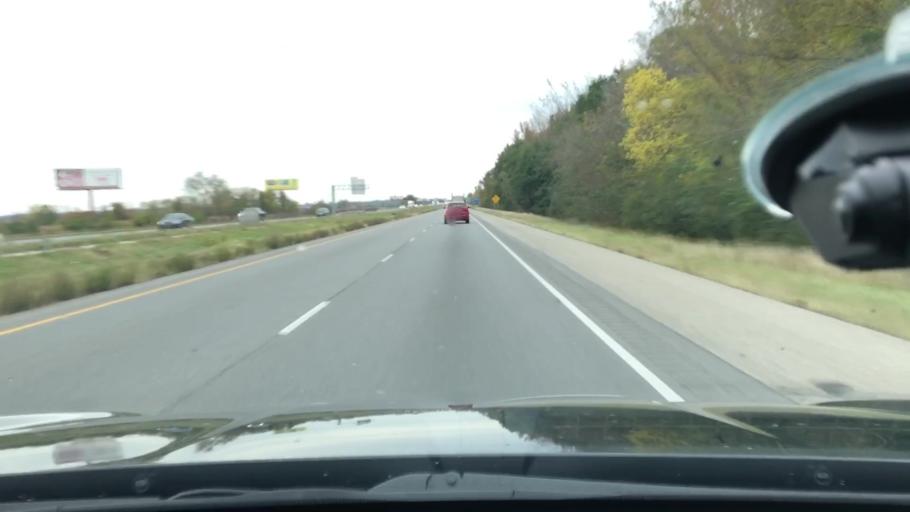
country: US
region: Arkansas
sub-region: Miller County
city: Texarkana
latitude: 33.4914
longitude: -93.9689
